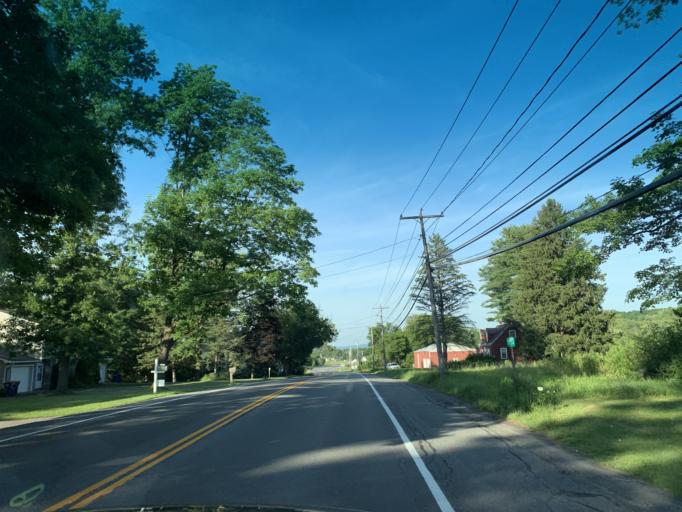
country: US
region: New York
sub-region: Oneida County
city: Clinton
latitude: 43.0670
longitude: -75.3510
